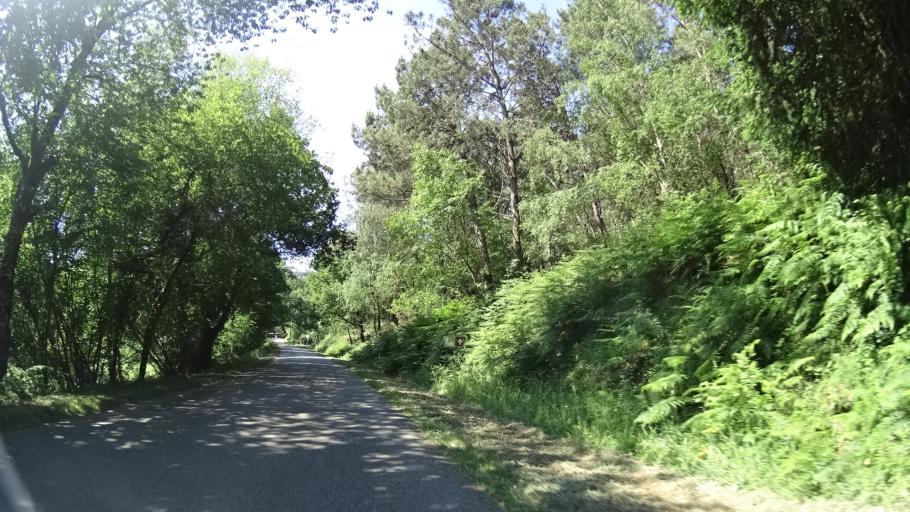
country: FR
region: Brittany
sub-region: Departement d'Ille-et-Vilaine
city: Langon
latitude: 47.7698
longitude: -1.8466
